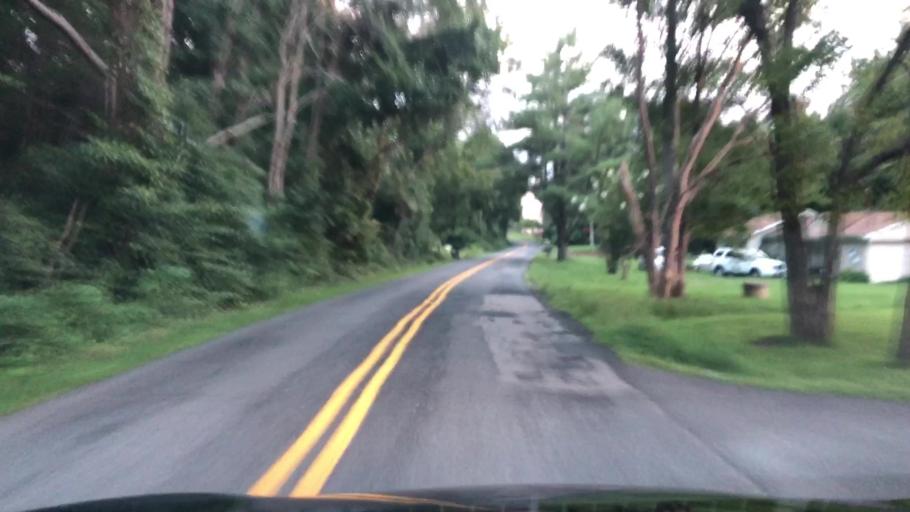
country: US
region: Virginia
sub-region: Stafford County
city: Stafford
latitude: 38.4731
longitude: -77.5785
